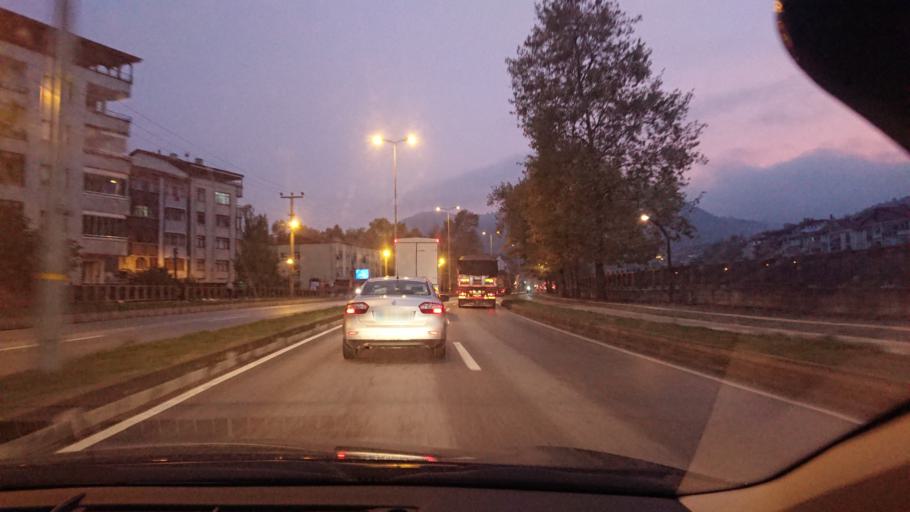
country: TR
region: Zonguldak
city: Devrek
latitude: 41.2231
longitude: 31.9584
